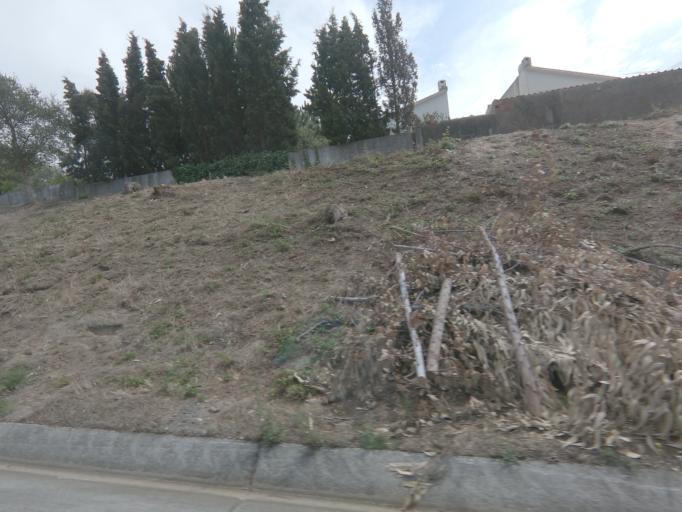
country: PT
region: Leiria
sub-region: Leiria
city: Leiria
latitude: 39.7625
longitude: -8.7948
